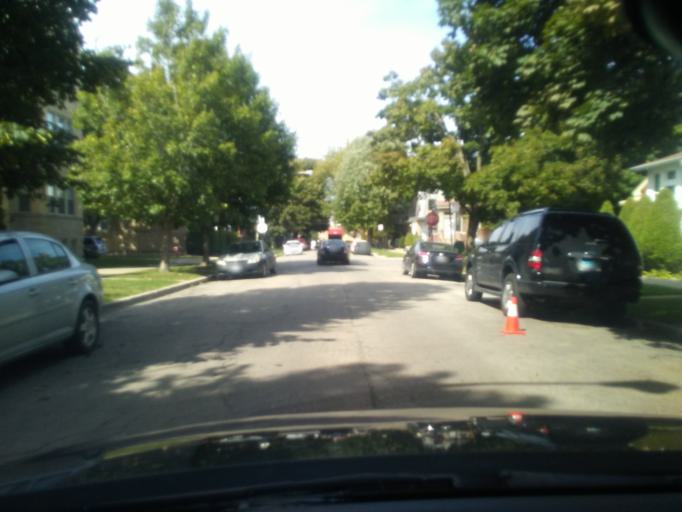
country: US
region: Illinois
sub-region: Cook County
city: Lincolnwood
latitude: 41.9354
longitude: -87.6953
